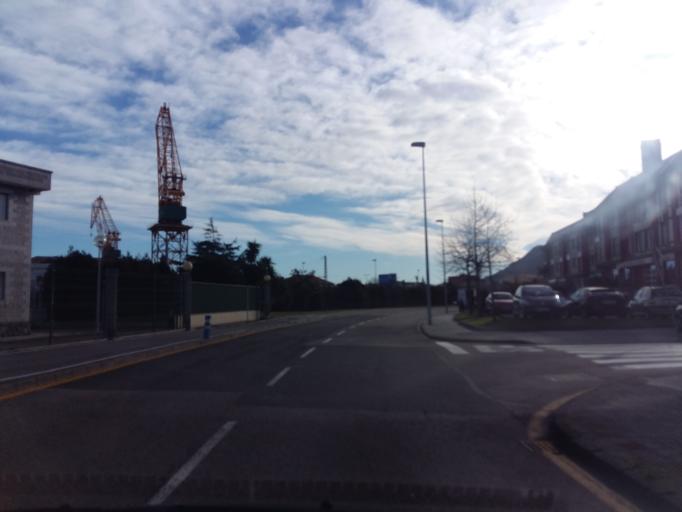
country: ES
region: Cantabria
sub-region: Provincia de Cantabria
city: El Astillero
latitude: 43.4033
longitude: -3.8208
